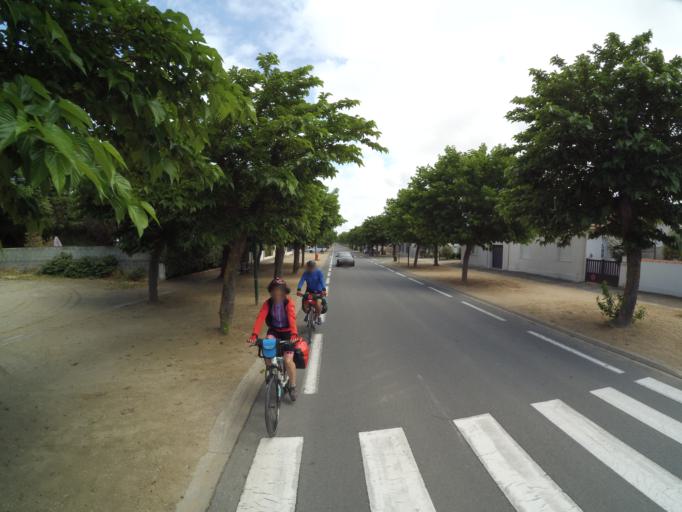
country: FR
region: Poitou-Charentes
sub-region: Departement de la Charente-Maritime
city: Chatelaillon-Plage
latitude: 46.0637
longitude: -1.0922
